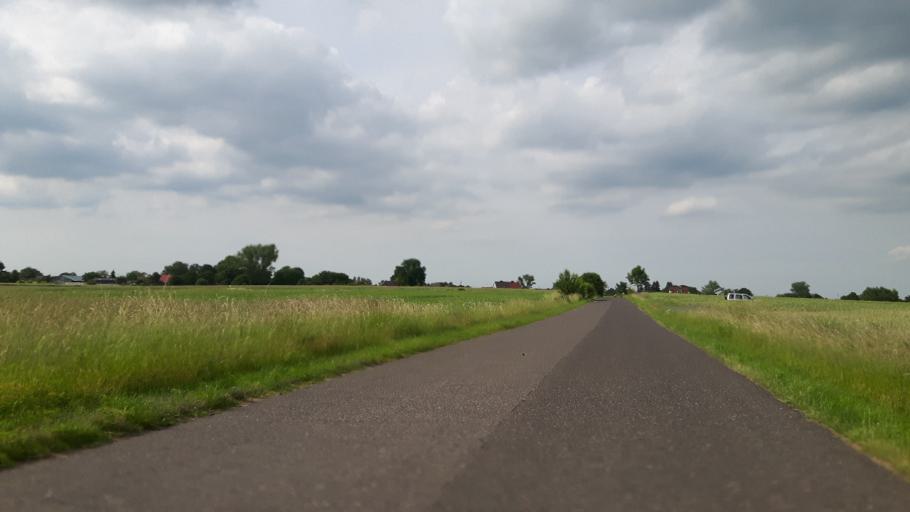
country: PL
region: West Pomeranian Voivodeship
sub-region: Powiat gryficki
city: Gryfice
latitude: 53.8097
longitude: 15.1286
